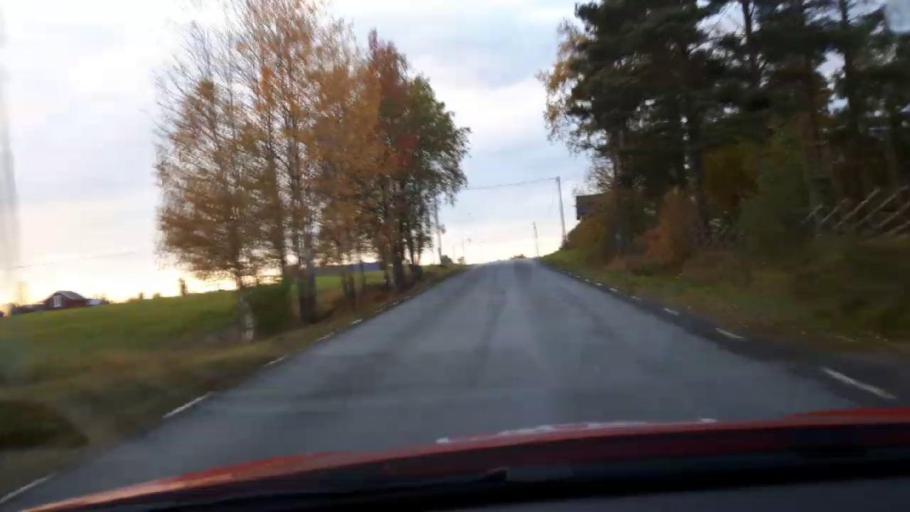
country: SE
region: Jaemtland
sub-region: OEstersunds Kommun
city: Lit
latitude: 63.3087
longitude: 14.9975
